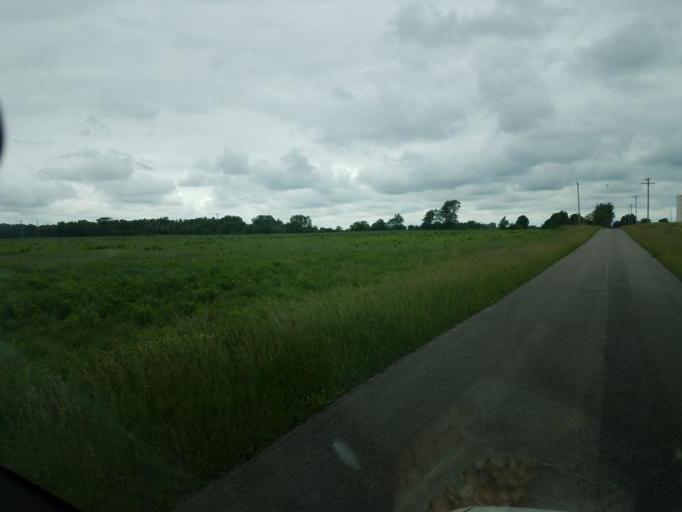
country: US
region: Ohio
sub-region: Morrow County
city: Cardington
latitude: 40.5684
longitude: -82.9035
